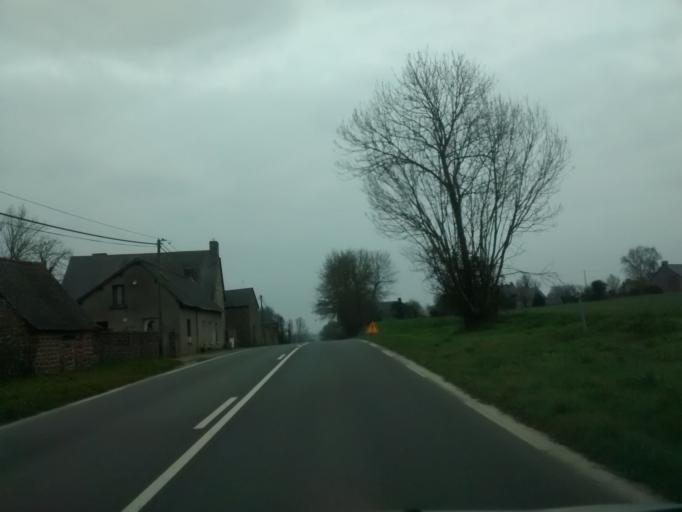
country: FR
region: Brittany
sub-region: Departement d'Ille-et-Vilaine
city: Sens-de-Bretagne
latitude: 48.3372
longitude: -1.5224
